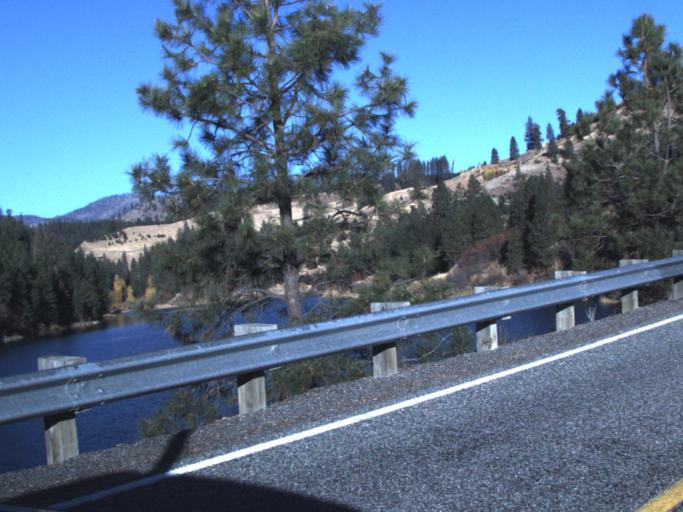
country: US
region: Washington
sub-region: Okanogan County
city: Coulee Dam
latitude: 48.0042
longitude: -118.6883
